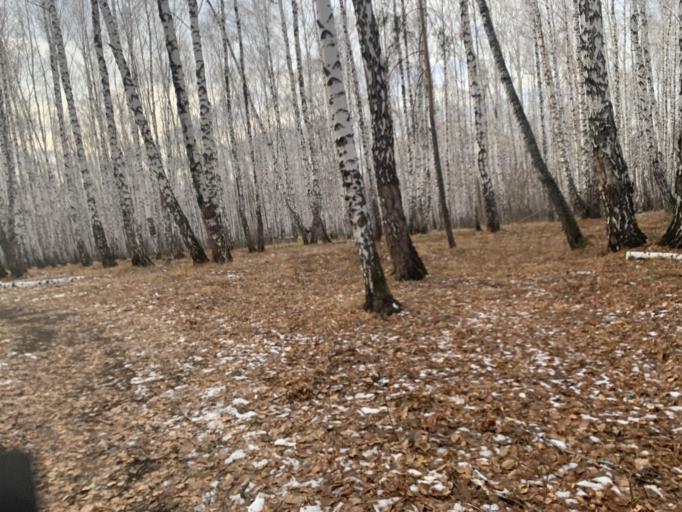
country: RU
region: Chelyabinsk
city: Roshchino
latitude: 55.2018
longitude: 61.3029
